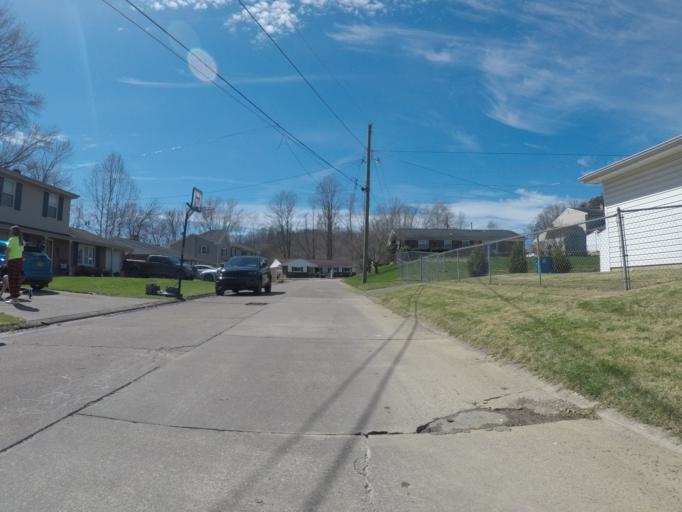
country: US
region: West Virginia
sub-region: Cabell County
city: Pea Ridge
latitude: 38.3986
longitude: -82.3187
